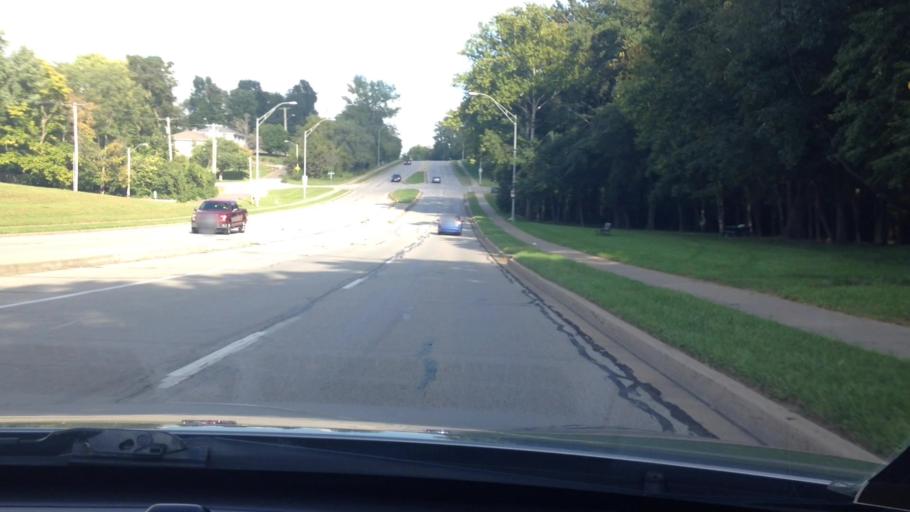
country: US
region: Missouri
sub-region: Clay County
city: Claycomo
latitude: 39.1803
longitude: -94.5050
